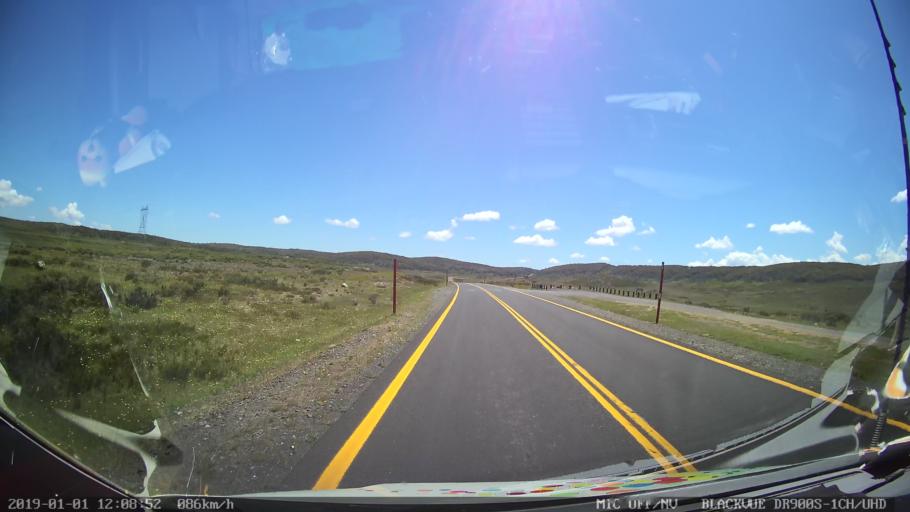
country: AU
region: New South Wales
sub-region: Tumut Shire
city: Tumut
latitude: -35.8147
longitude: 148.4963
